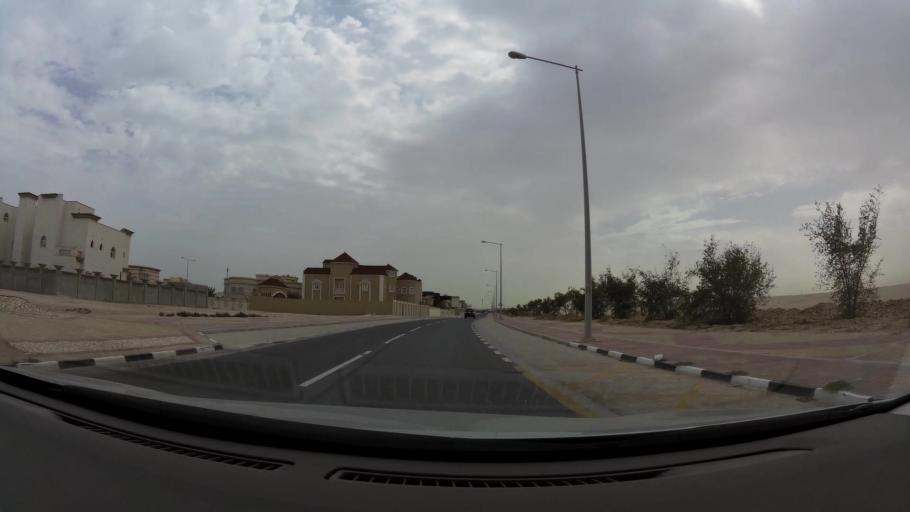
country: QA
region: Baladiyat ad Dawhah
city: Doha
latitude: 25.3557
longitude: 51.4935
